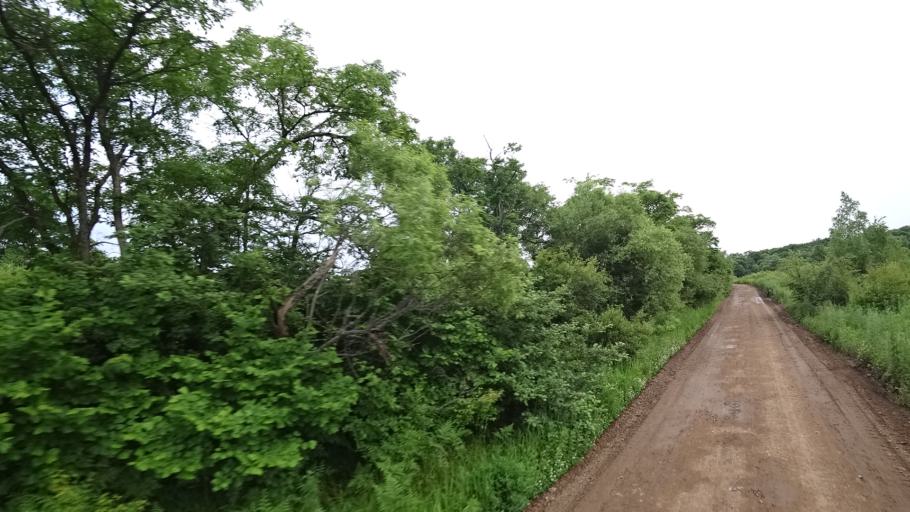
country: RU
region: Primorskiy
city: Novosysoyevka
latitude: 44.2342
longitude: 133.3798
